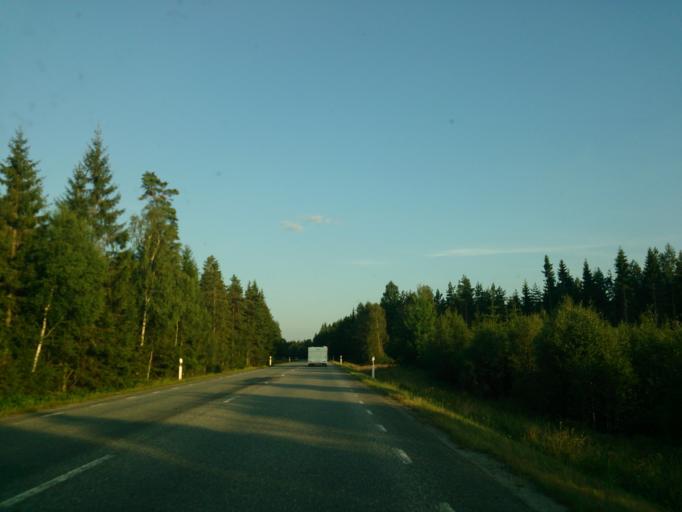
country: SE
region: Joenkoeping
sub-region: Varnamo Kommun
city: Varnamo
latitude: 57.1538
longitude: 14.0885
